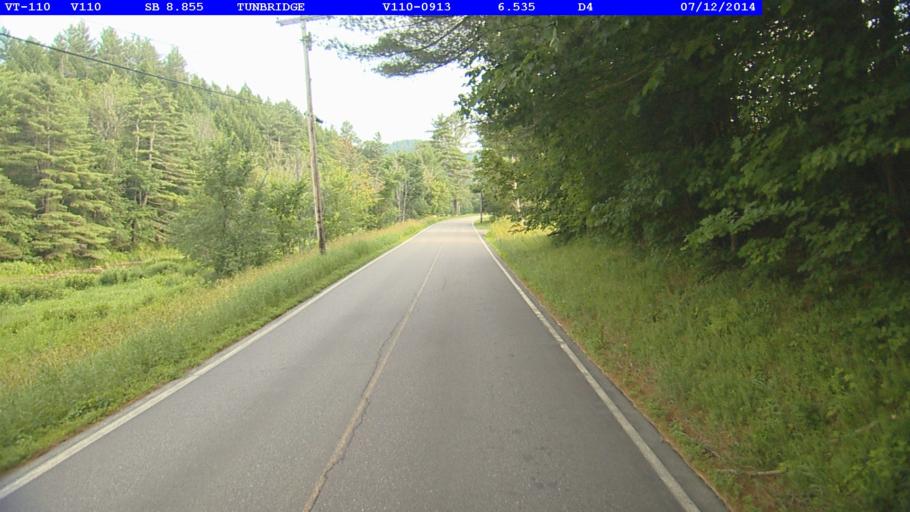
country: US
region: Vermont
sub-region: Orange County
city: Chelsea
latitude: 43.9336
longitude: -72.4664
